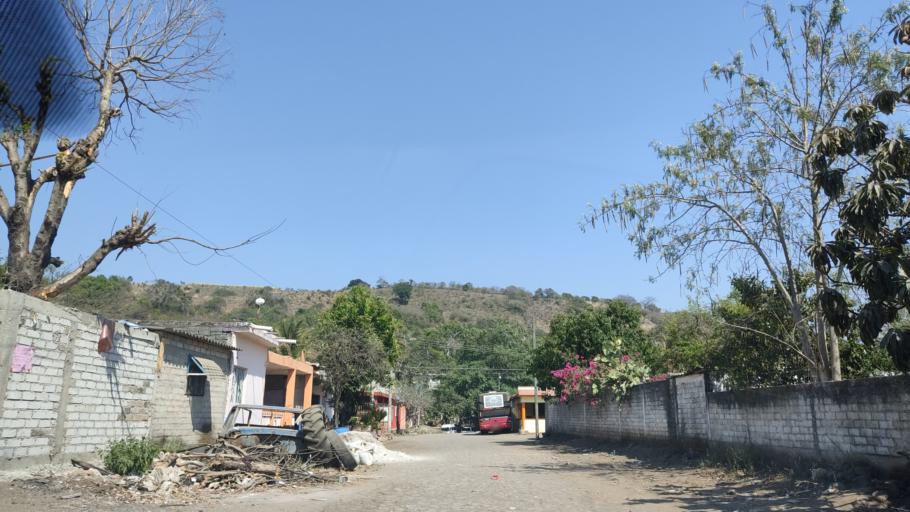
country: MX
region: Nayarit
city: Puga
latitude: 21.5307
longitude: -104.8056
